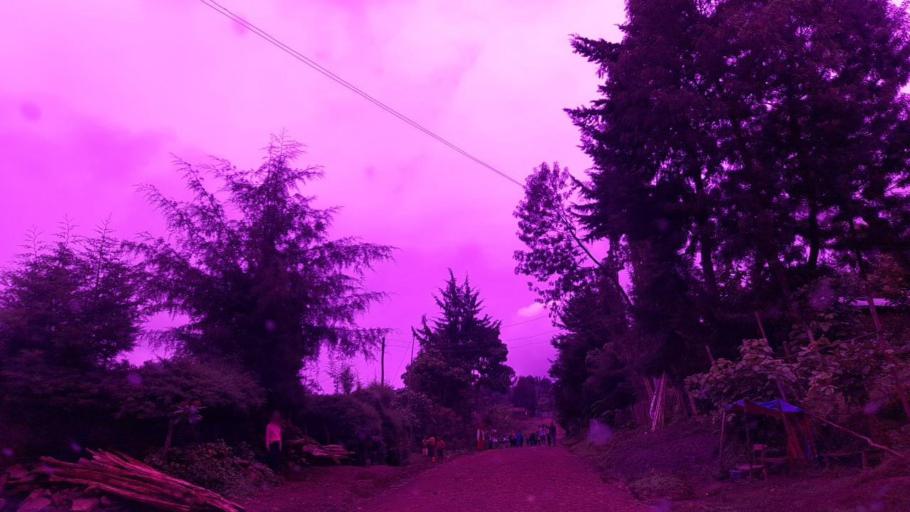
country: ET
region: Southern Nations, Nationalities, and People's Region
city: Tippi
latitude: 7.5919
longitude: 35.7646
